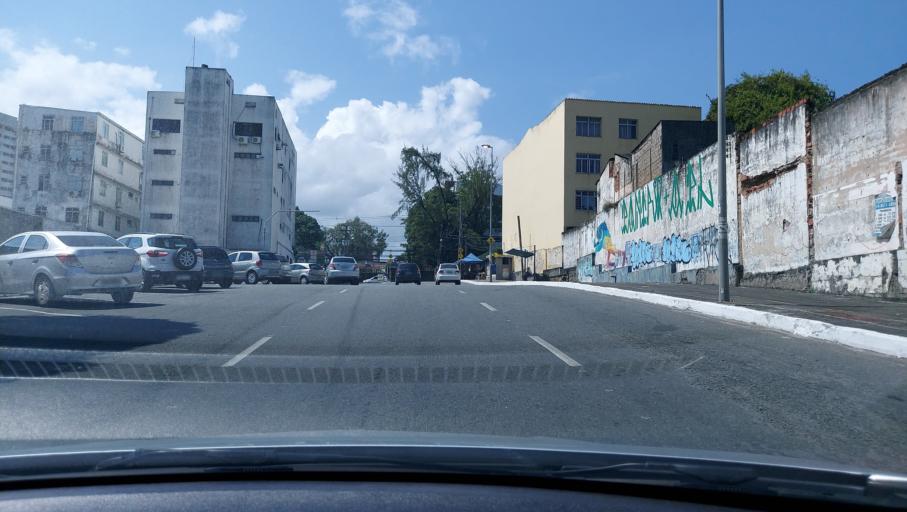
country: BR
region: Bahia
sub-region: Salvador
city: Salvador
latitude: -12.9663
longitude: -38.4715
